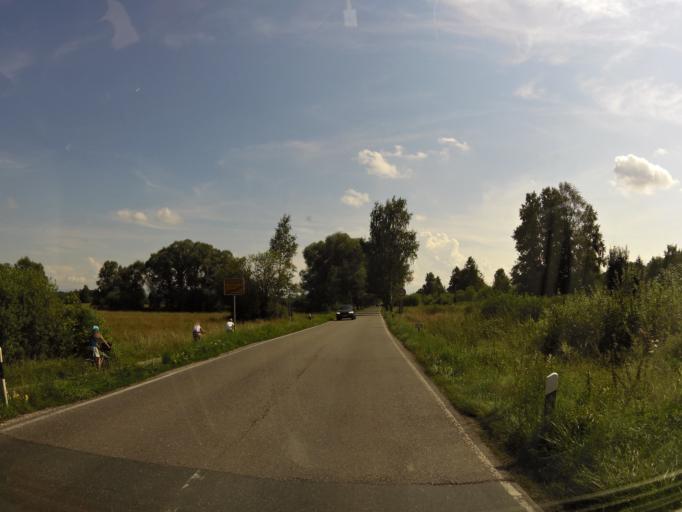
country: DE
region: Bavaria
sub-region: Upper Bavaria
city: Diessen am Ammersee
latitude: 47.9401
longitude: 11.1069
